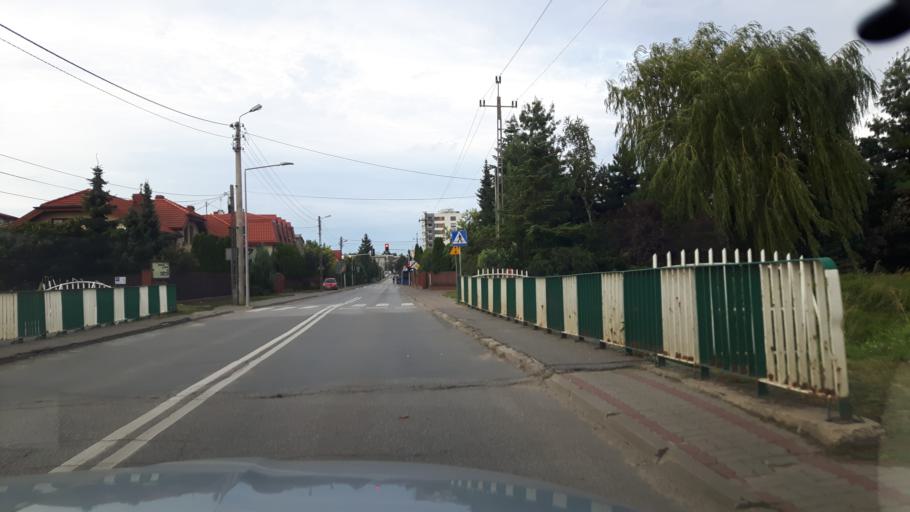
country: PL
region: Masovian Voivodeship
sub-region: Powiat wolominski
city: Marki
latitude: 52.3254
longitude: 21.0992
